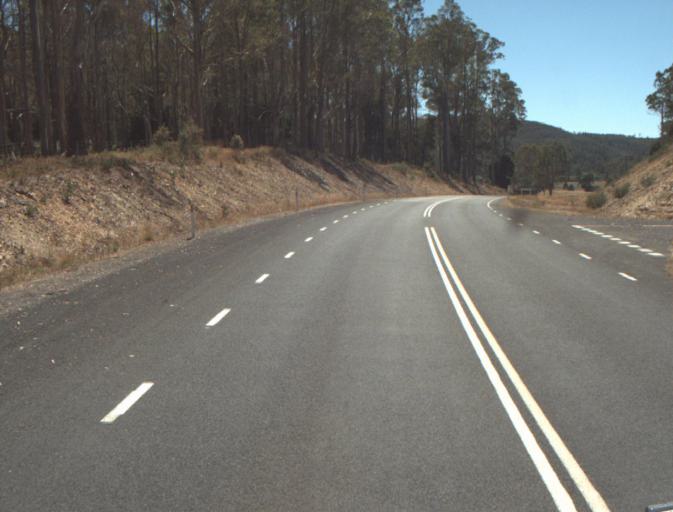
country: AU
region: Tasmania
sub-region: Launceston
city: Newstead
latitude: -41.3367
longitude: 147.3474
